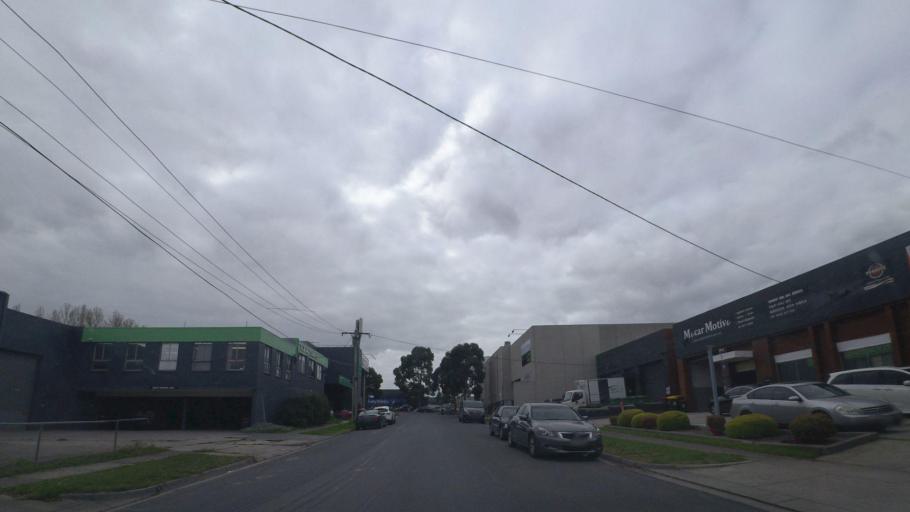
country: AU
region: Victoria
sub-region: Whitehorse
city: Nunawading
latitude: -37.8194
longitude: 145.1726
